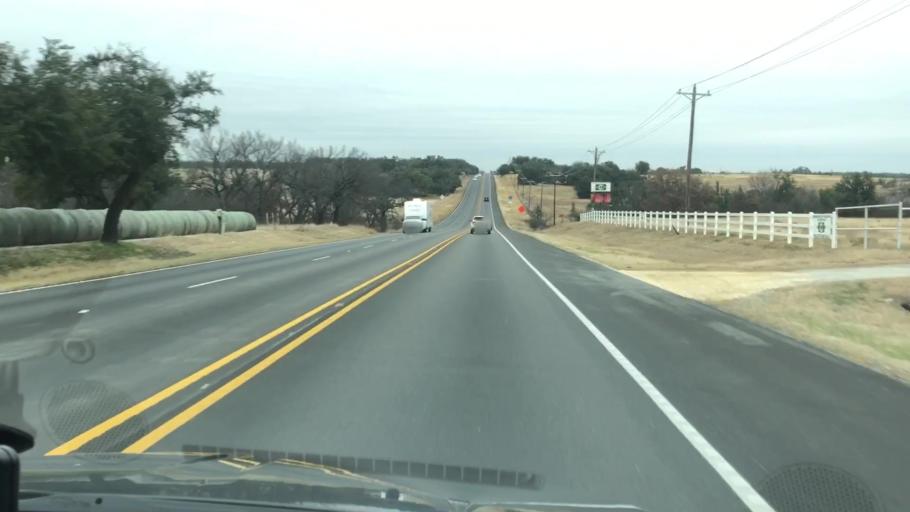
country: US
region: Texas
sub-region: Erath County
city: Stephenville
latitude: 32.3006
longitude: -98.1877
